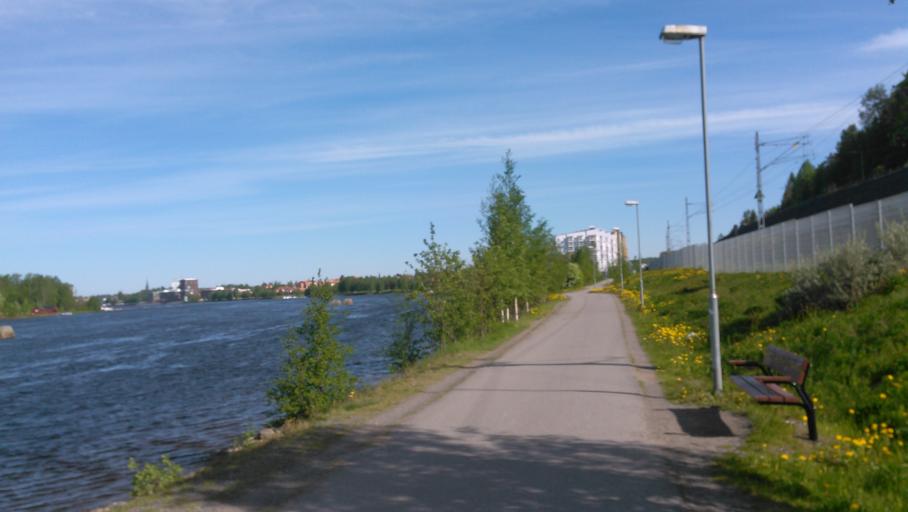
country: SE
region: Vaesterbotten
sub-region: Umea Kommun
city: Umea
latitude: 63.8099
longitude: 20.2956
